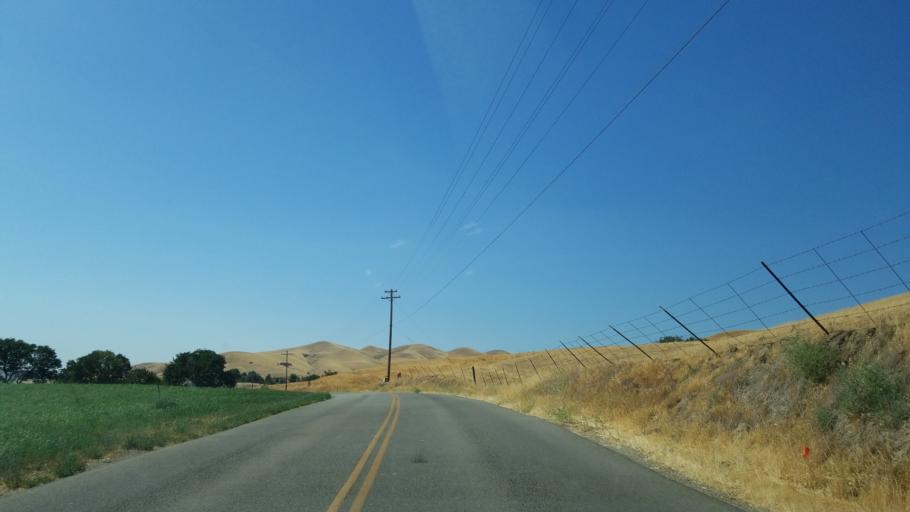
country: US
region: California
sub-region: San Luis Obispo County
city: San Miguel
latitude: 35.7677
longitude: -120.6877
